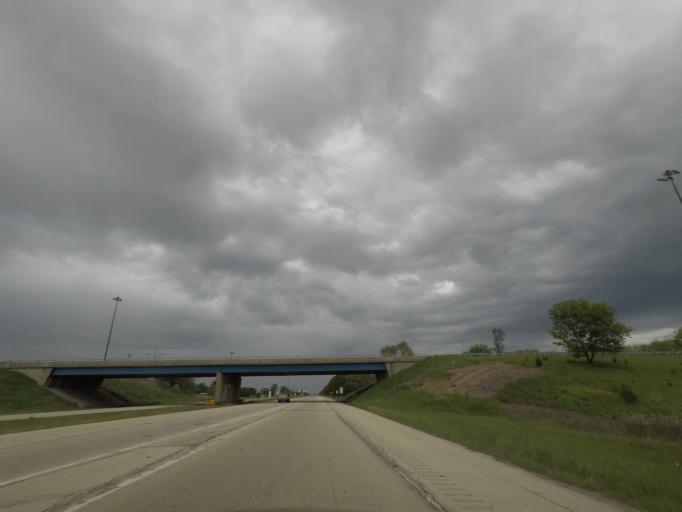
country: US
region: Illinois
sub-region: Winnebago County
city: Cherry Valley
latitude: 42.2202
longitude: -89.0104
